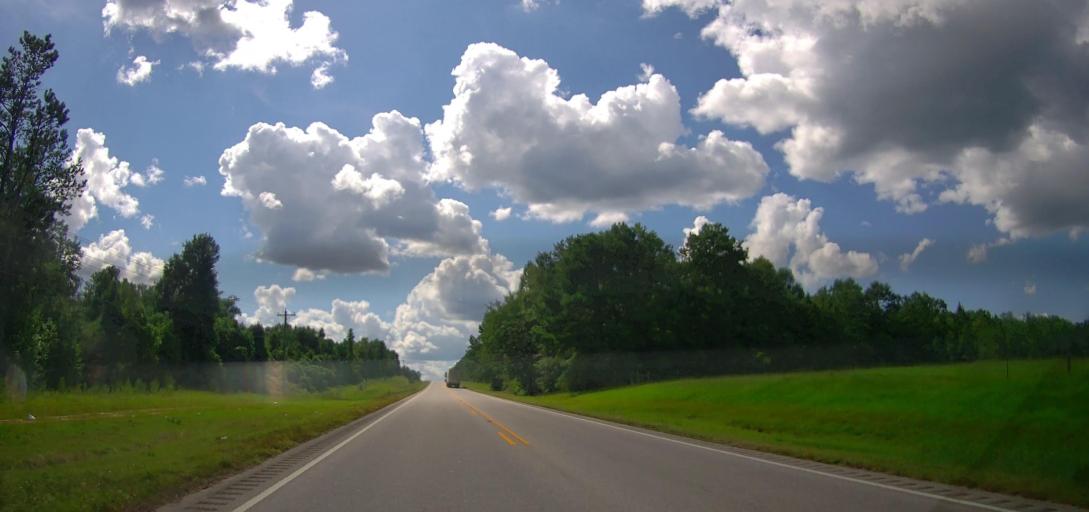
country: US
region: Alabama
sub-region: Macon County
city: Tuskegee
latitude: 32.4541
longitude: -85.5364
